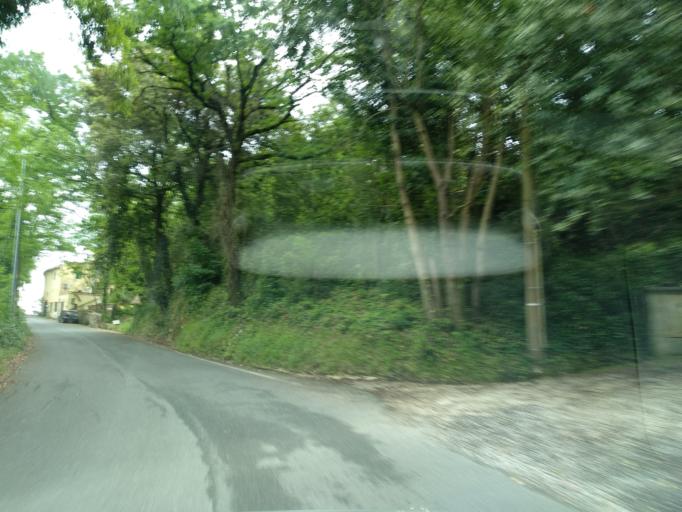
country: IT
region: Tuscany
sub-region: Provincia di Livorno
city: Guasticce
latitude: 43.5436
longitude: 10.4353
